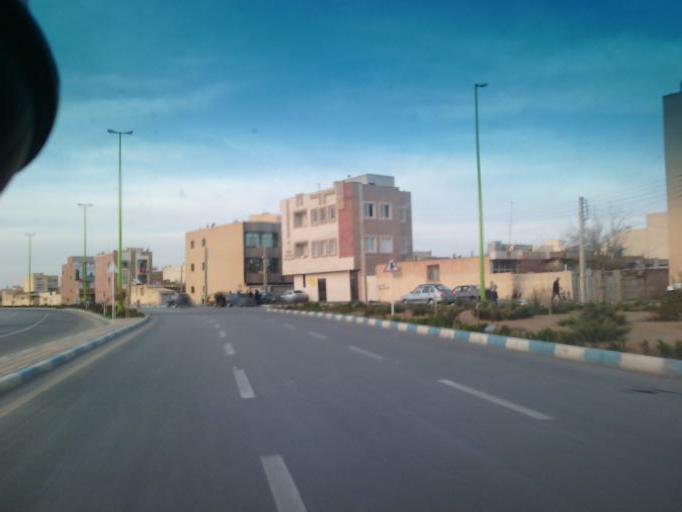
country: IR
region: Isfahan
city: Shahin Shahr
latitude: 32.8700
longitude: 51.5424
